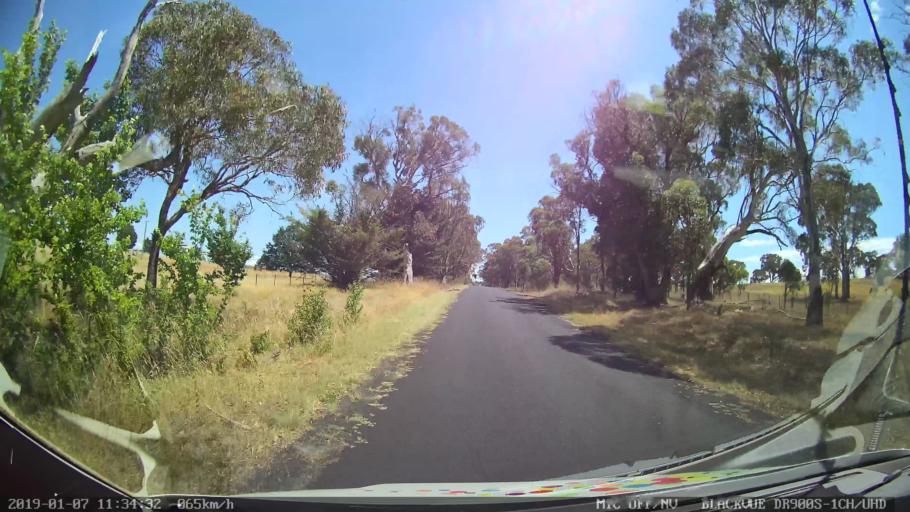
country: AU
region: New South Wales
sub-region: Armidale Dumaresq
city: Armidale
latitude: -30.3891
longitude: 151.5584
